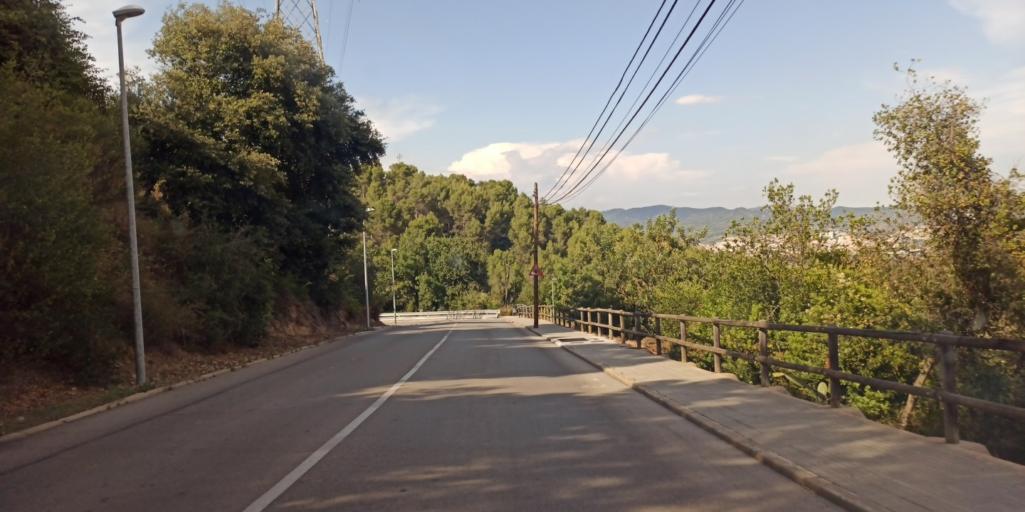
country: ES
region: Catalonia
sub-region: Provincia de Barcelona
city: Santa Coloma de Cervello
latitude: 41.3604
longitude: 2.0064
